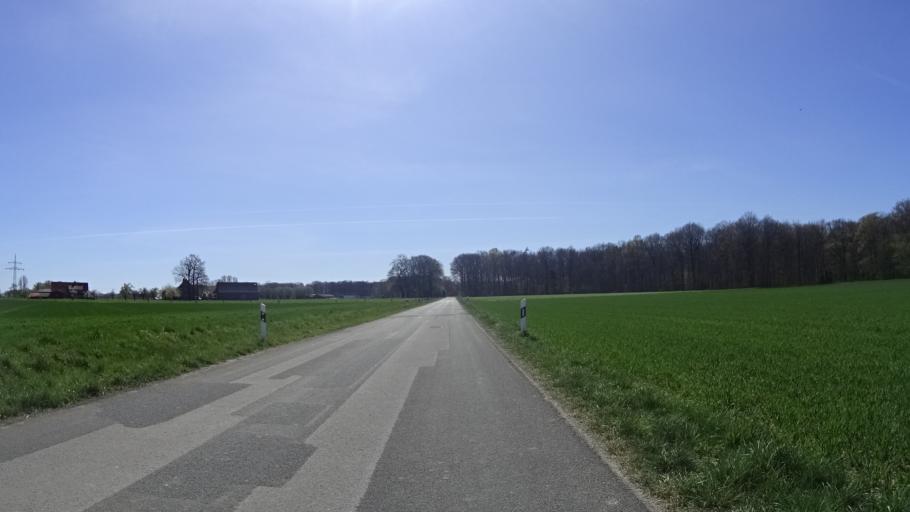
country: DE
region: North Rhine-Westphalia
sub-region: Regierungsbezirk Munster
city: Dulmen
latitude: 51.8142
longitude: 7.3494
